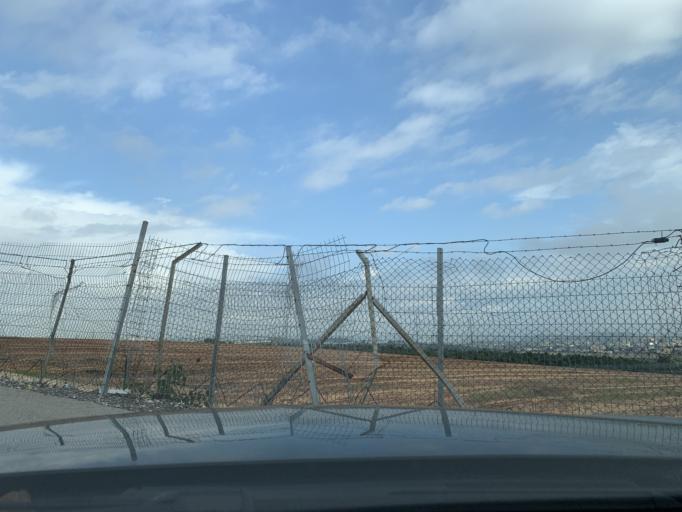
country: PS
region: West Bank
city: Qalqilyah
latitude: 32.1987
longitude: 34.9515
